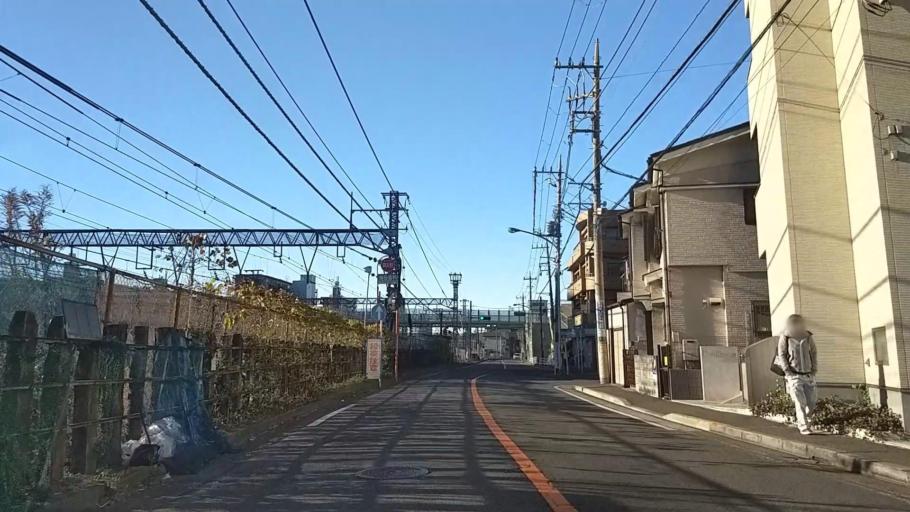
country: JP
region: Kanagawa
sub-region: Kawasaki-shi
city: Kawasaki
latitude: 35.5017
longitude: 139.6734
